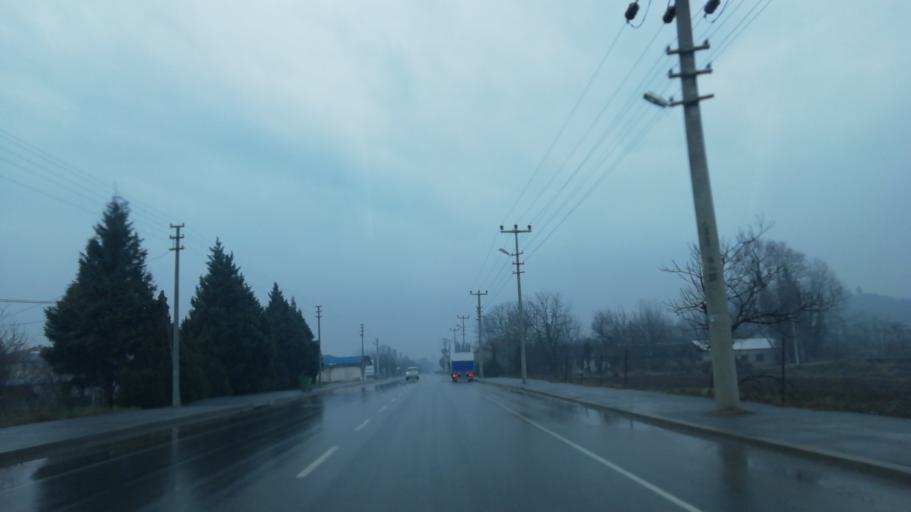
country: TR
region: Sakarya
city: Akyazi
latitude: 40.6459
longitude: 30.6209
